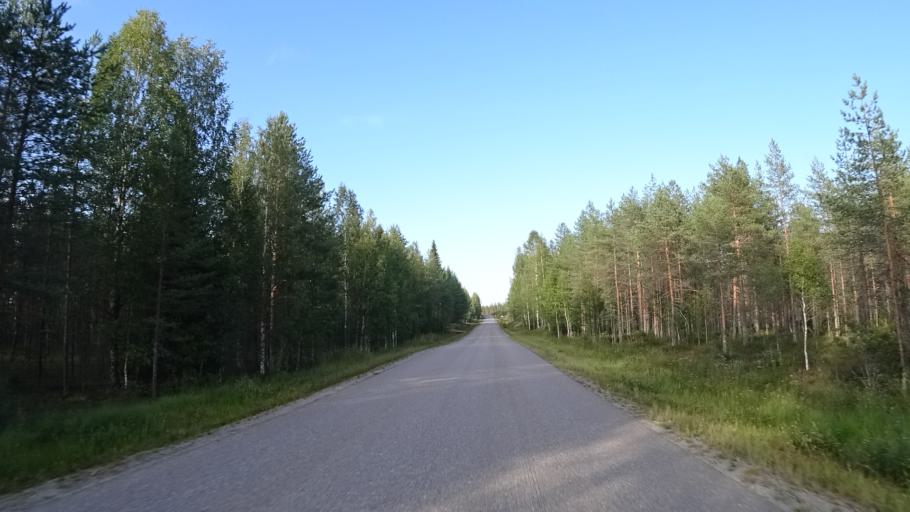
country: FI
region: North Karelia
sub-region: Joensuu
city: Eno
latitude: 63.0626
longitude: 30.5506
